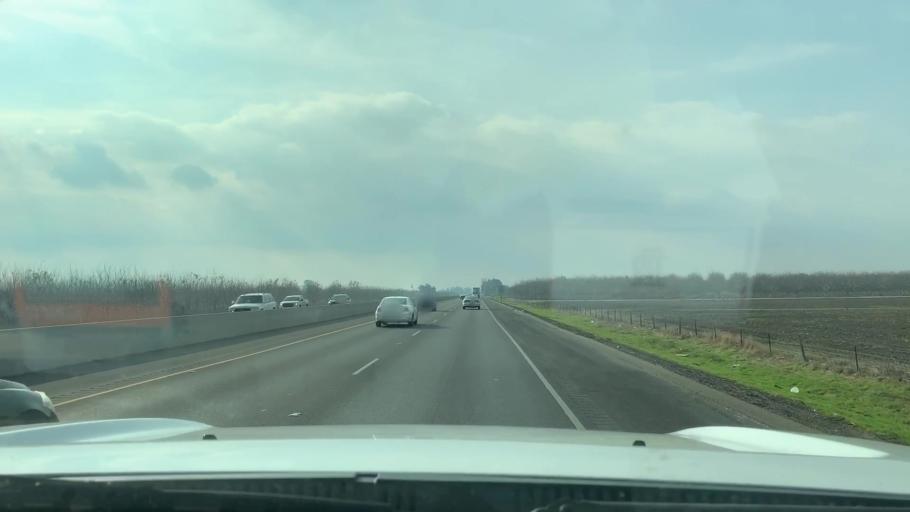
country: US
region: California
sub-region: Kings County
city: Armona
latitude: 36.3075
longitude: -119.7154
